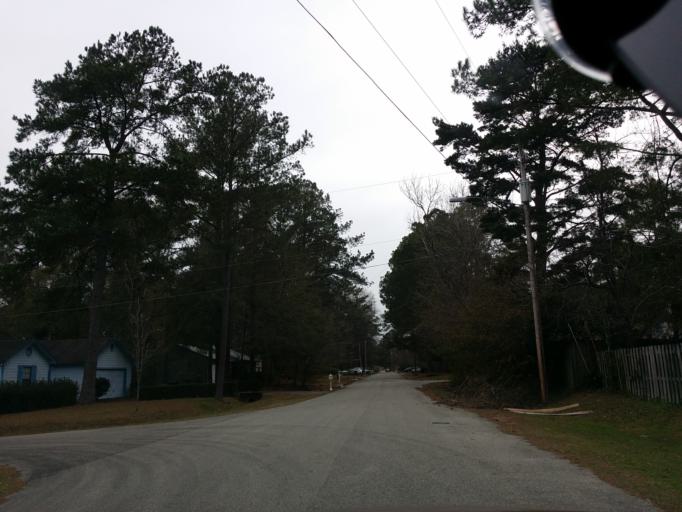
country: US
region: Florida
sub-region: Leon County
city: Tallahassee
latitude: 30.5016
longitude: -84.2200
